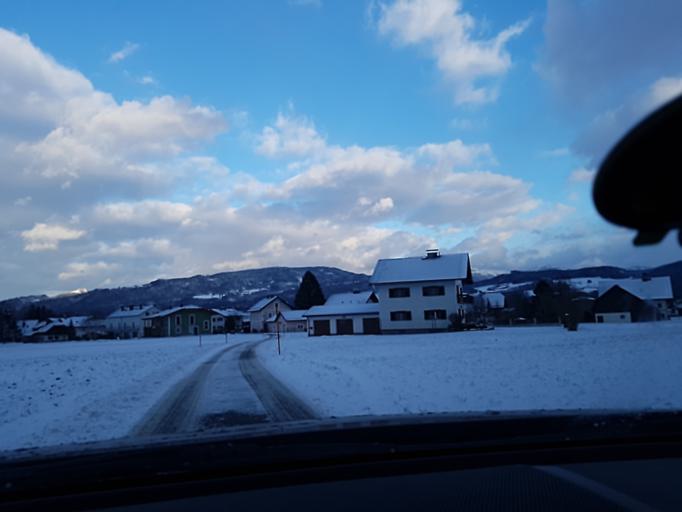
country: AT
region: Salzburg
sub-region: Politischer Bezirk Salzburg-Umgebung
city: Grodig
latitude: 47.7209
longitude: 13.0582
